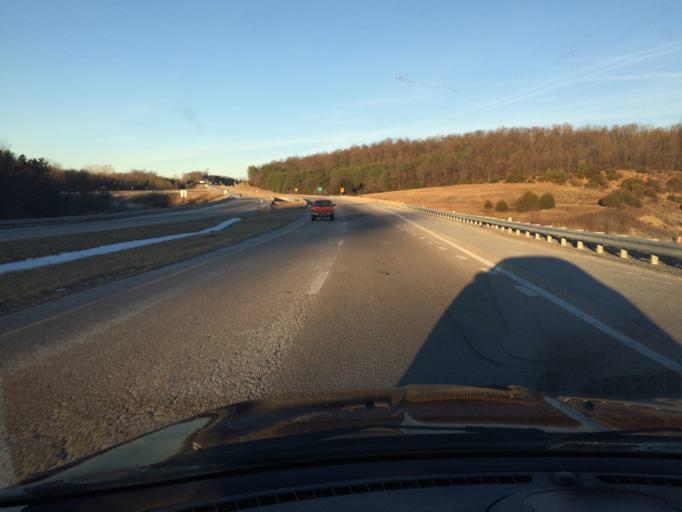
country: US
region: Virginia
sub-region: Augusta County
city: Jolivue
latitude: 38.1257
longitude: -79.0739
